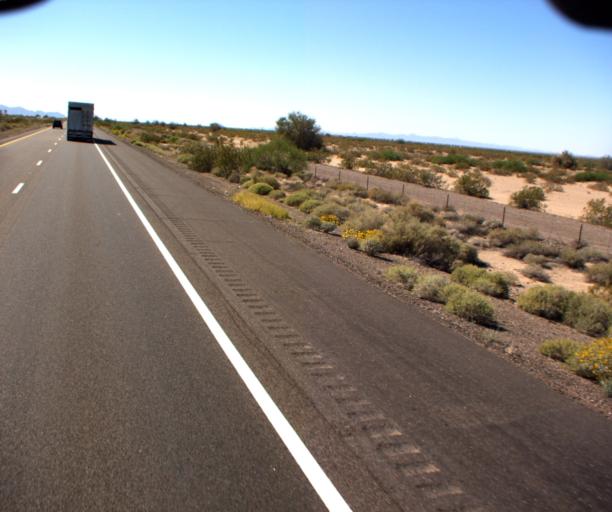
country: US
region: Arizona
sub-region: Yuma County
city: Wellton
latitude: 32.8203
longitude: -113.4770
